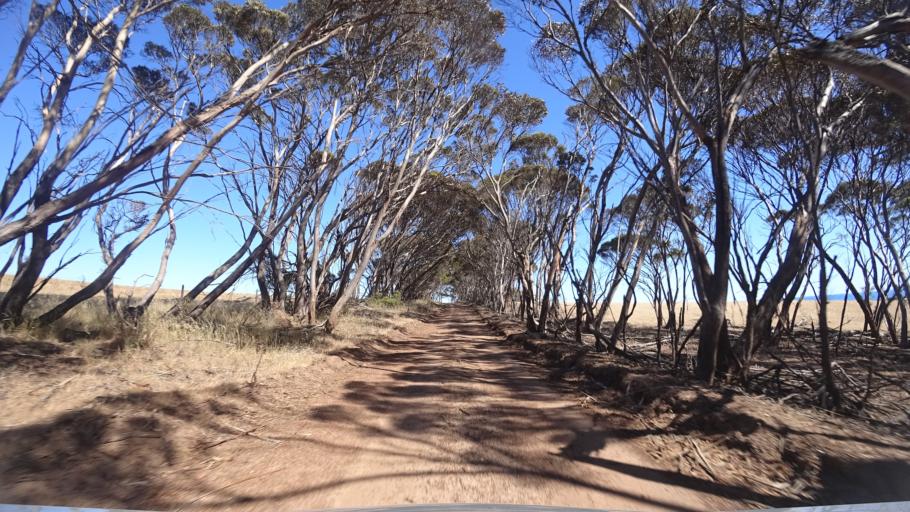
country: AU
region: South Australia
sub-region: Kangaroo Island
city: Kingscote
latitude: -35.7461
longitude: 137.7238
